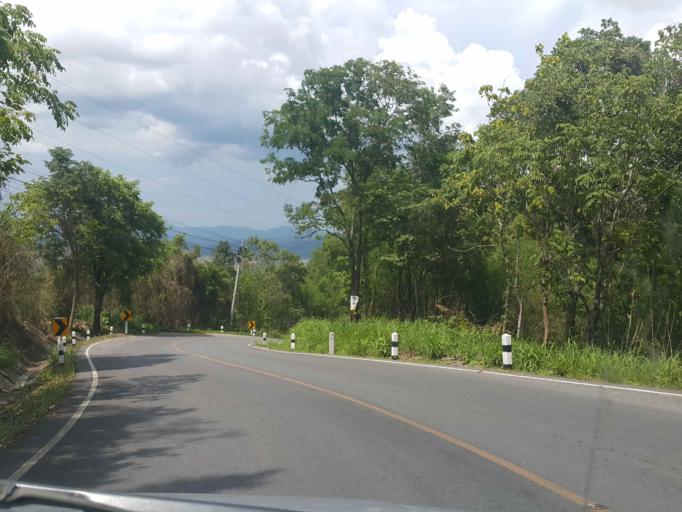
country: TH
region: Nan
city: Ban Luang
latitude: 18.8763
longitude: 100.5365
